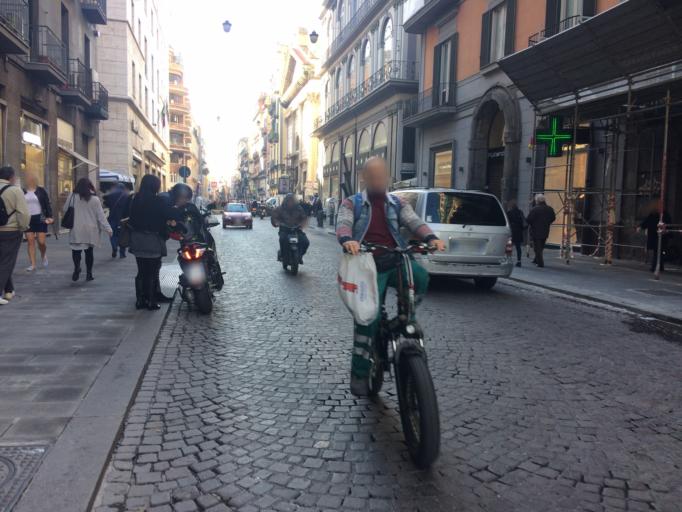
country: IT
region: Campania
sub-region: Provincia di Napoli
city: Napoli
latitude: 40.8434
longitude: 14.2490
